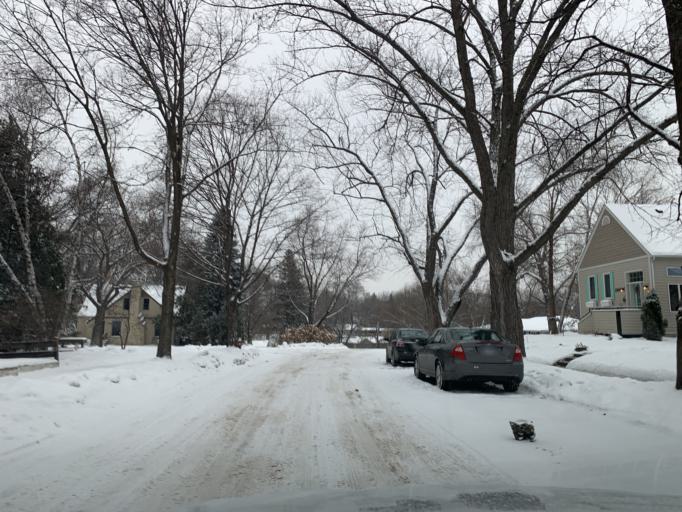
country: US
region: Minnesota
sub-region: Hennepin County
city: Saint Louis Park
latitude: 44.9498
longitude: -93.3391
